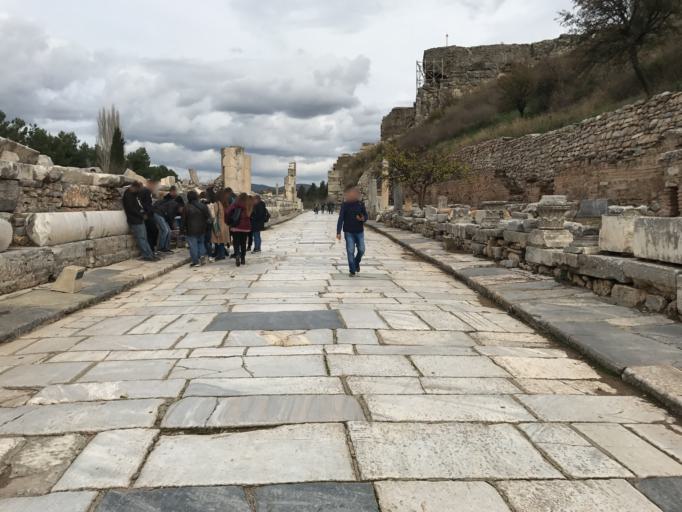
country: TR
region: Izmir
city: Selcuk
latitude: 37.9397
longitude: 27.3416
